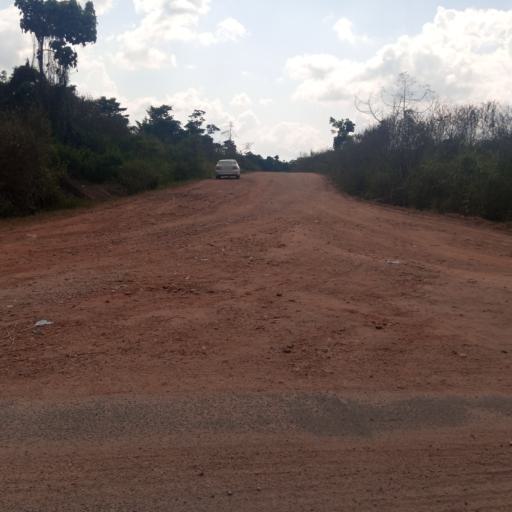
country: NG
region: Osun
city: Modakeke
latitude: 7.1304
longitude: 4.4115
